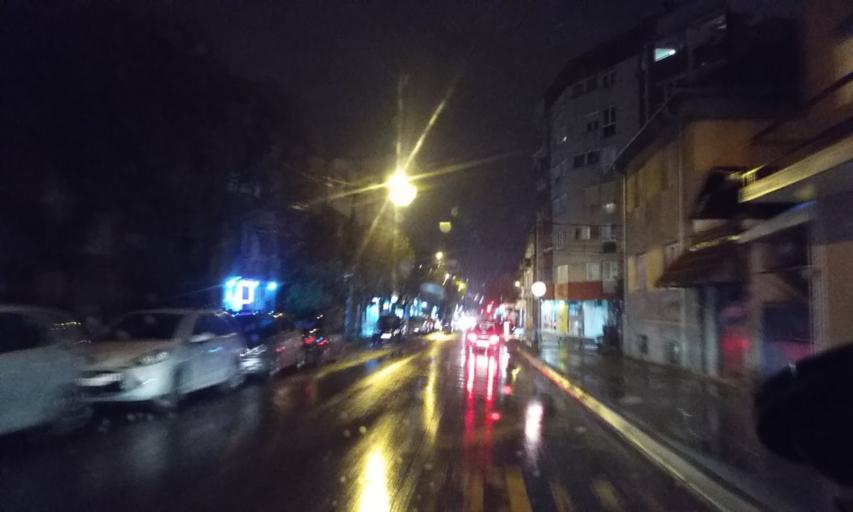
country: RS
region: Central Serbia
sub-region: Nisavski Okrug
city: Nis
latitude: 43.3121
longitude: 21.9005
